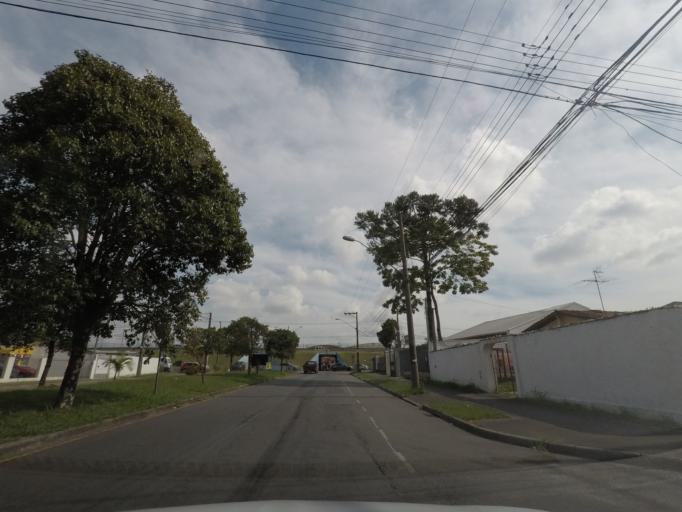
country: BR
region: Parana
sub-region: Pinhais
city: Pinhais
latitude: -25.4725
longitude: -49.2092
